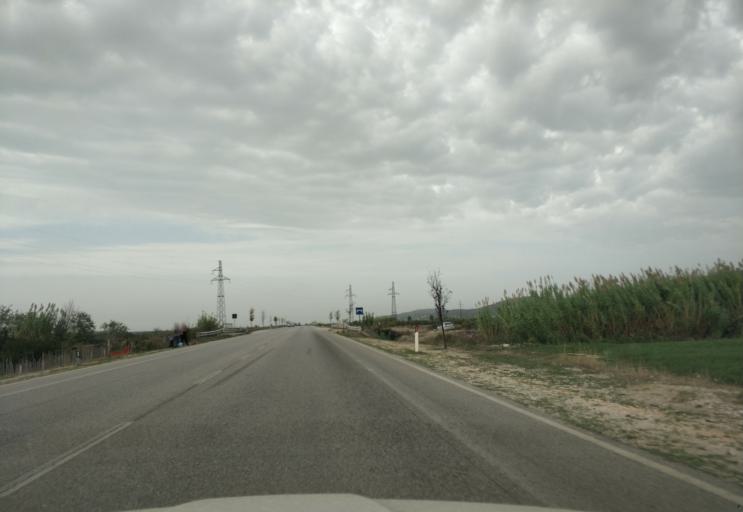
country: AL
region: Fier
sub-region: Rrethi i Fierit
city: Frakulla e Madhe
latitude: 40.6391
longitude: 19.5026
